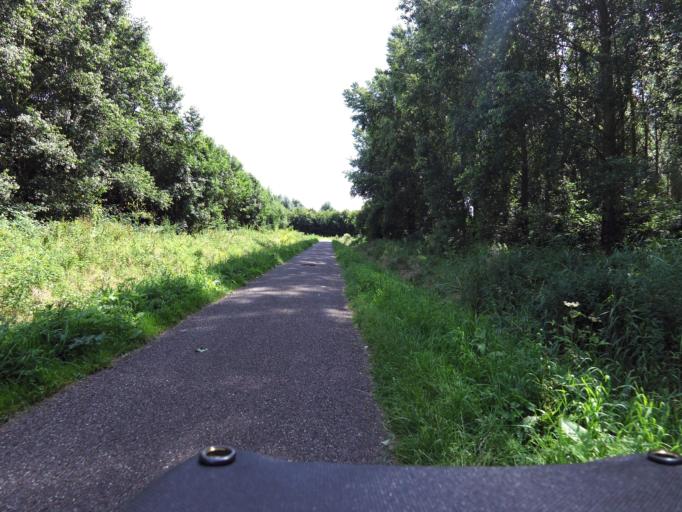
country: NL
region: South Holland
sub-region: Gemeente Albrandswaard
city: Rhoon
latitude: 51.8651
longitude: 4.3887
